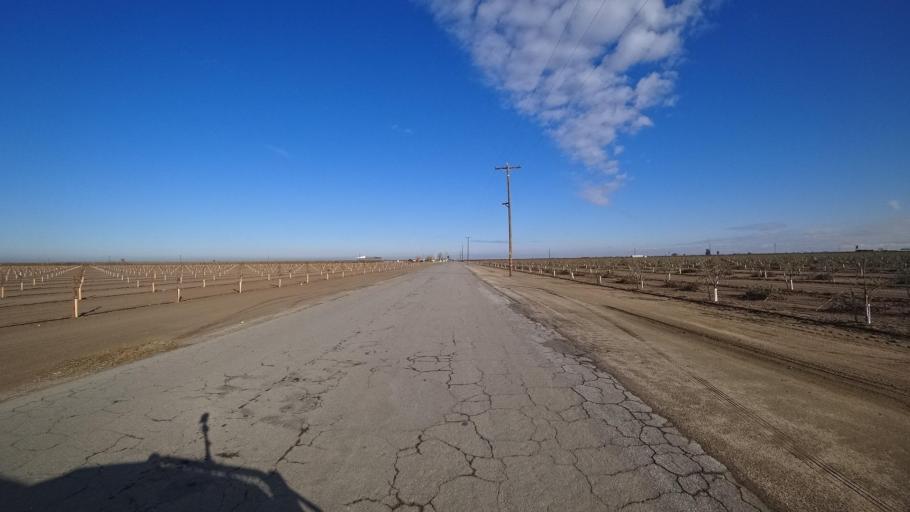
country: US
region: California
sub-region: Kern County
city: Delano
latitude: 35.7147
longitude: -119.3030
